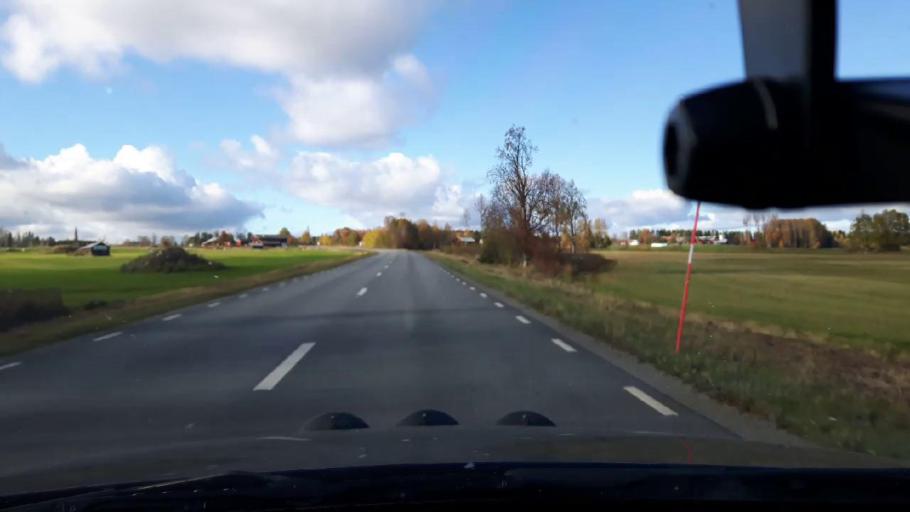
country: SE
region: Jaemtland
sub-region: Bergs Kommun
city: Hoverberg
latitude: 62.9886
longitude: 14.4325
